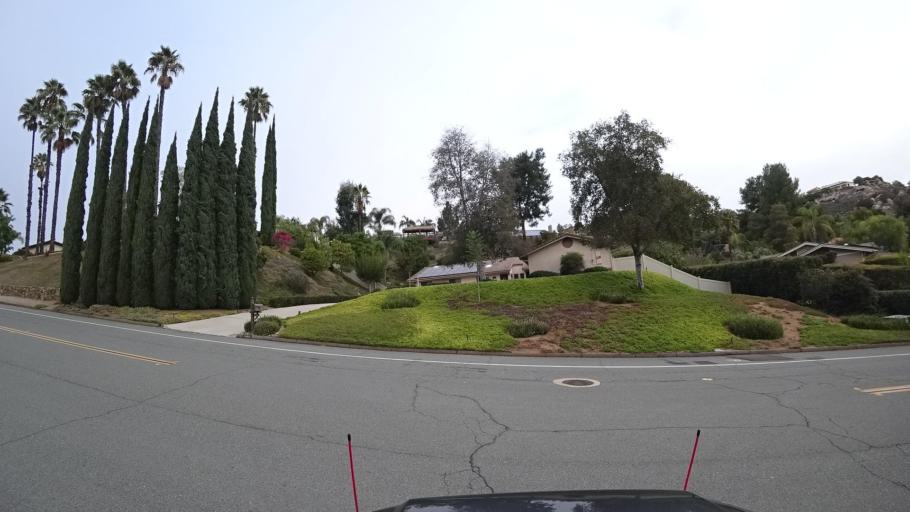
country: US
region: California
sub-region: San Diego County
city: Granite Hills
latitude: 32.7742
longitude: -116.9130
